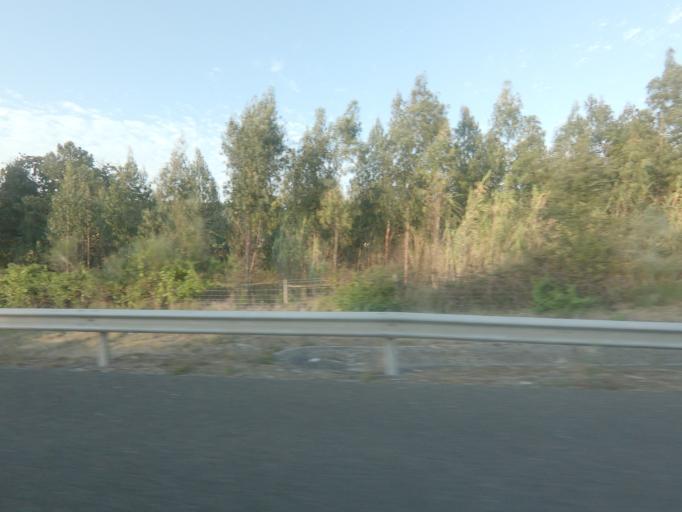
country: PT
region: Leiria
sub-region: Leiria
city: Santa Catarina da Serra
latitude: 39.7070
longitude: -8.7068
